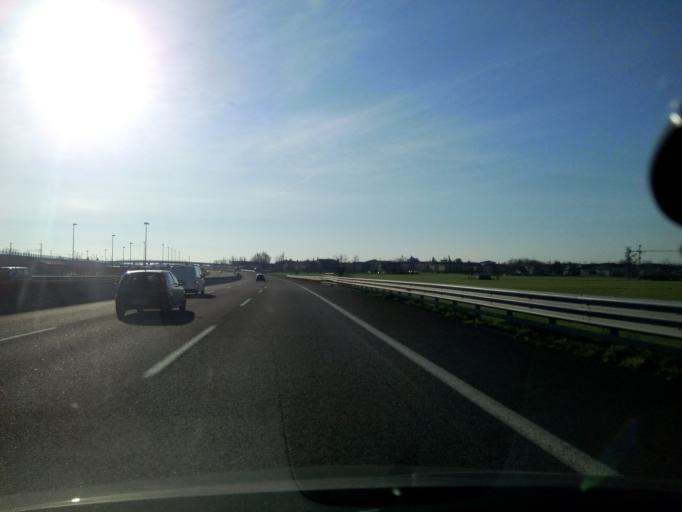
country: IT
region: Emilia-Romagna
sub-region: Provincia di Reggio Emilia
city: Roncocesi
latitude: 44.7438
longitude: 10.5706
